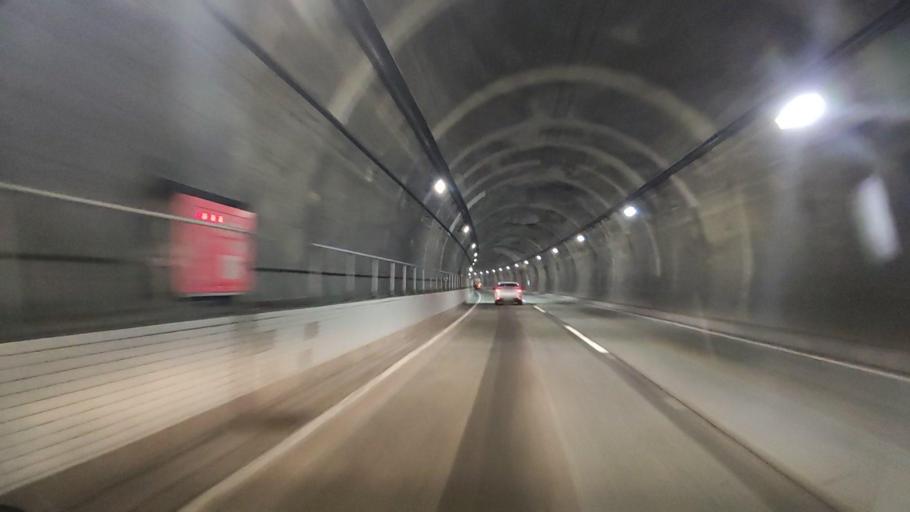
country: JP
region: Iwate
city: Ichinohe
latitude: 40.2345
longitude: 141.3931
